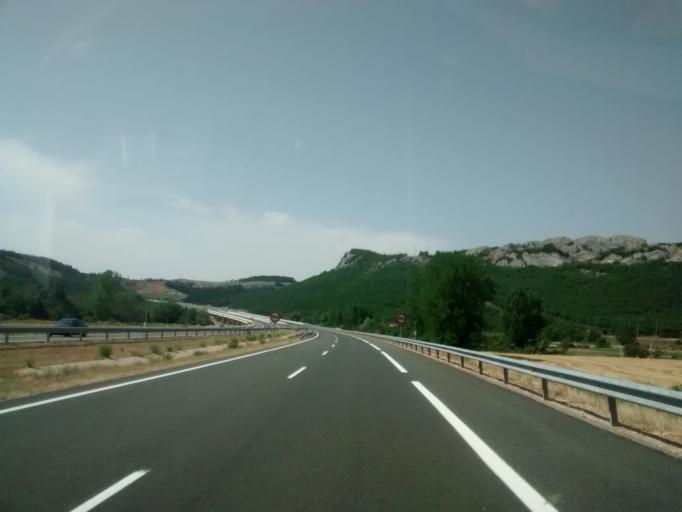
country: ES
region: Castille and Leon
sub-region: Provincia de Palencia
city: Alar del Rey
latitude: 42.6994
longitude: -4.2953
